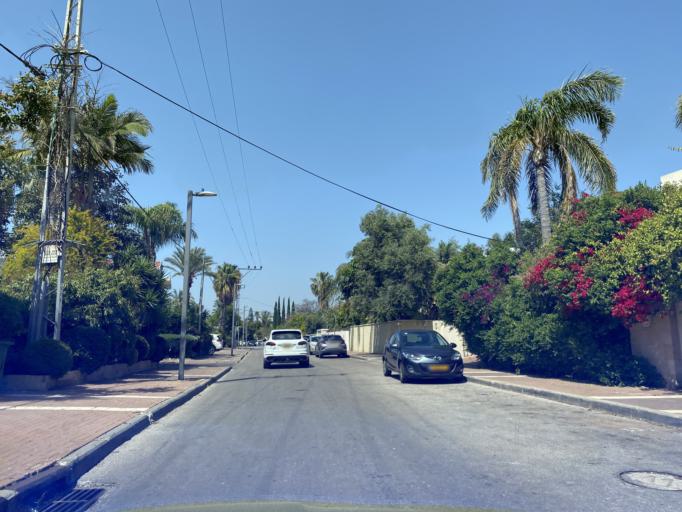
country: IL
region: Tel Aviv
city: Herzliya Pituah
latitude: 32.1751
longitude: 34.8138
